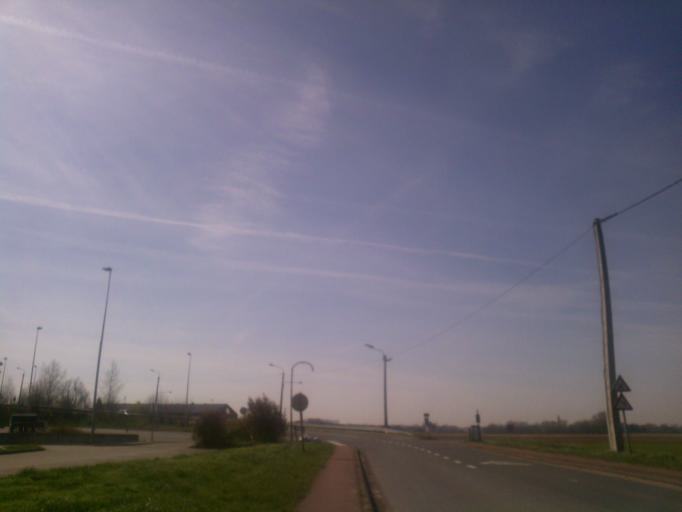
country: BE
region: Wallonia
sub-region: Province du Hainaut
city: Silly
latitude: 50.6642
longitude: 3.9350
